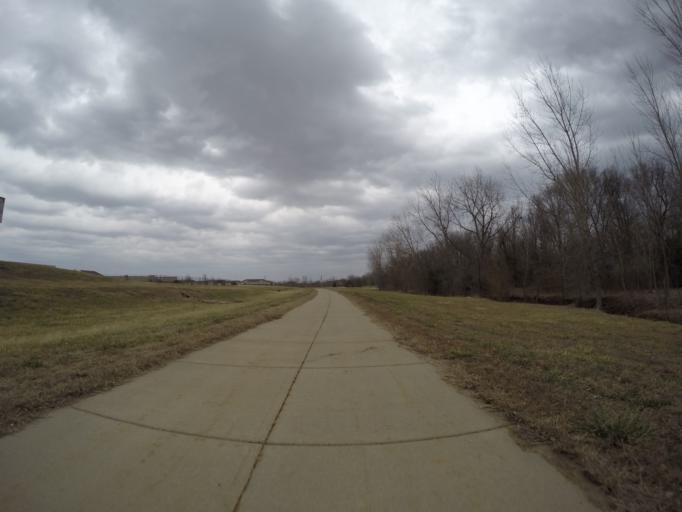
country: US
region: Kansas
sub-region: Riley County
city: Manhattan
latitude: 39.2114
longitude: -96.6106
